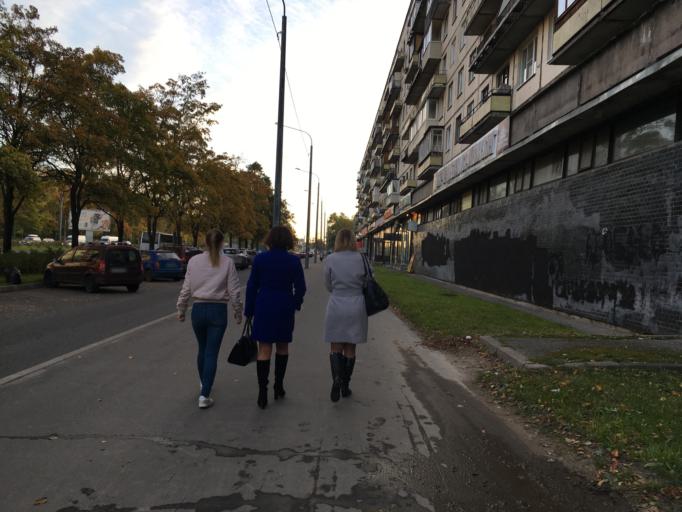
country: RU
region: St.-Petersburg
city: Grazhdanka
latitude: 60.0373
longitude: 30.3961
